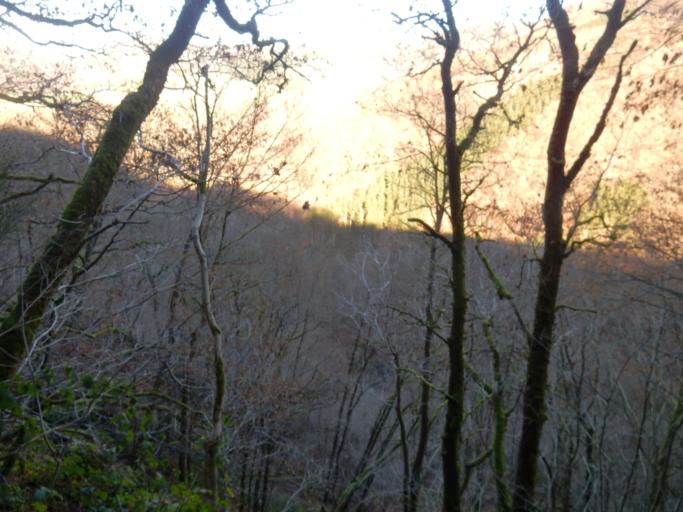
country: LU
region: Diekirch
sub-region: Canton de Diekirch
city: Bourscheid
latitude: 49.9177
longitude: 6.0703
